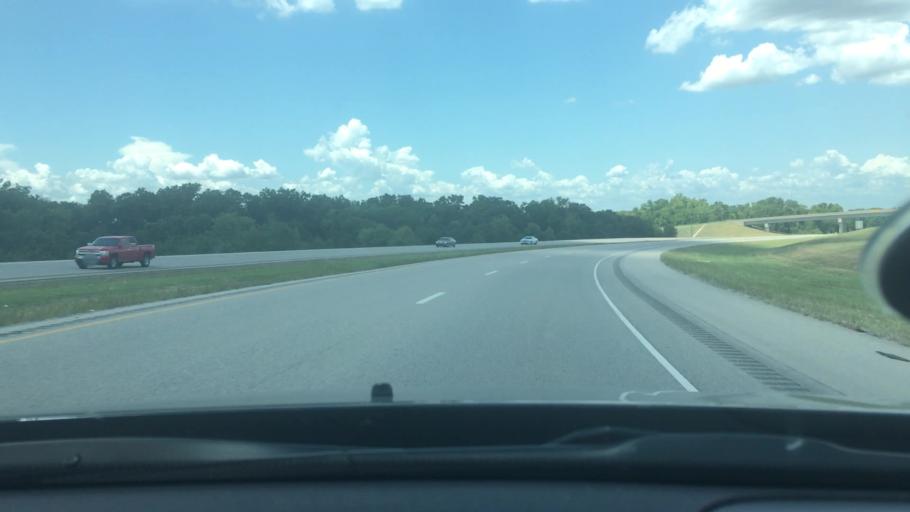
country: US
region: Oklahoma
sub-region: Bryan County
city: Calera
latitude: 33.9796
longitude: -96.4268
